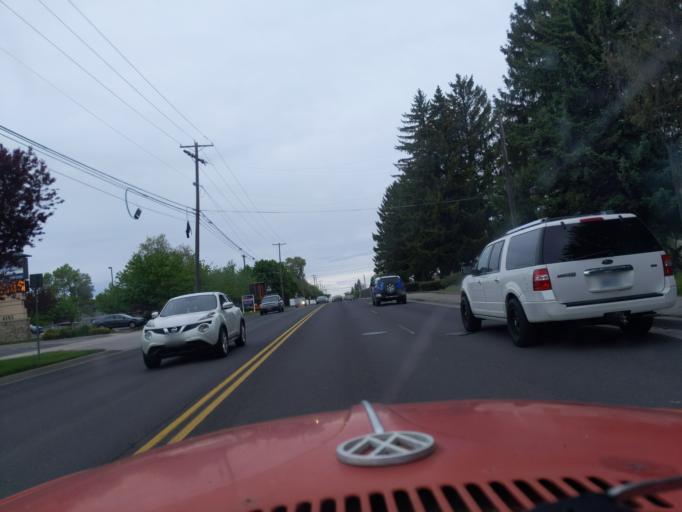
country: US
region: Washington
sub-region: Spokane County
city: Spokane
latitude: 47.6162
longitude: -117.3686
